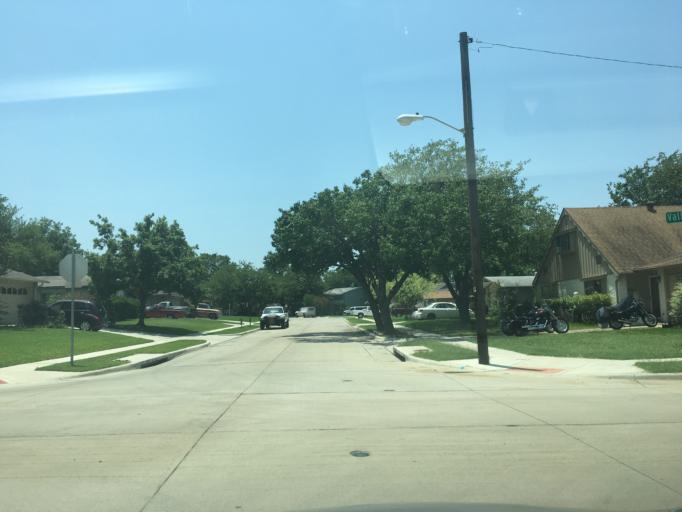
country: US
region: Texas
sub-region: Dallas County
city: Carrollton
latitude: 32.9490
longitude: -96.8743
